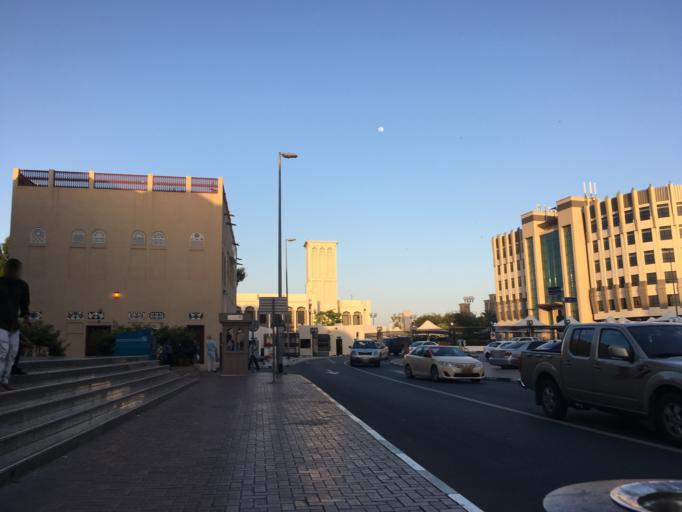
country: AE
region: Ash Shariqah
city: Sharjah
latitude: 25.2642
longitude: 55.2969
